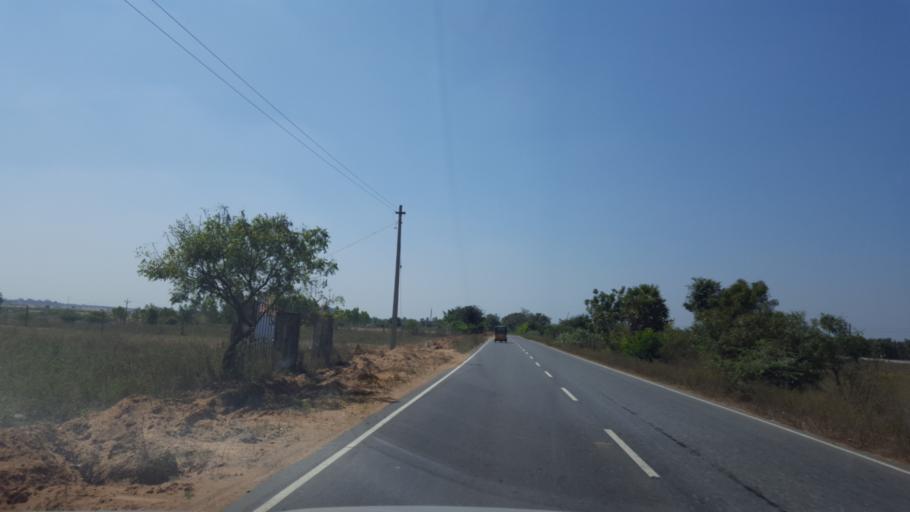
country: IN
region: Tamil Nadu
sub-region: Kancheepuram
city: Wallajahbad
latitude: 12.7725
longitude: 79.8907
